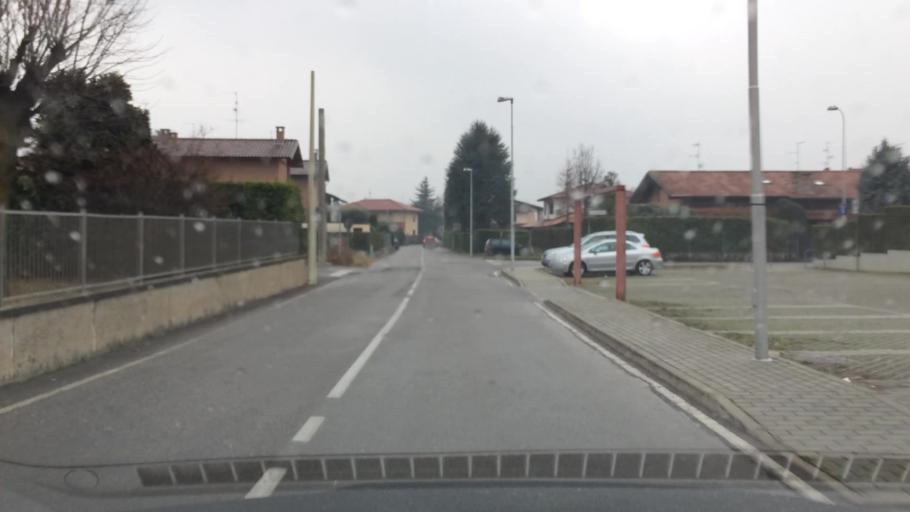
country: IT
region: Lombardy
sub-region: Provincia di Como
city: San Michele-San Giorgio
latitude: 45.6936
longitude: 9.0569
